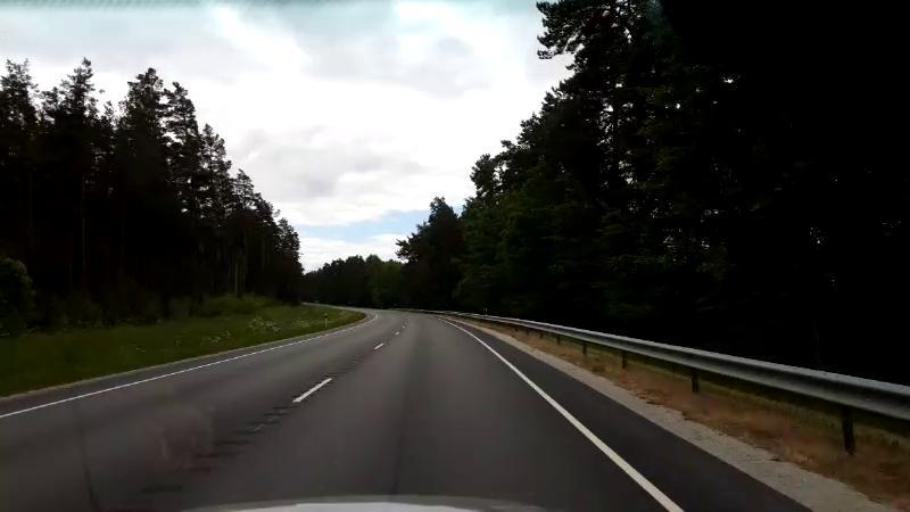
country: EE
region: Paernumaa
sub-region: Paernu linn
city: Parnu
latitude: 58.1511
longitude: 24.4994
